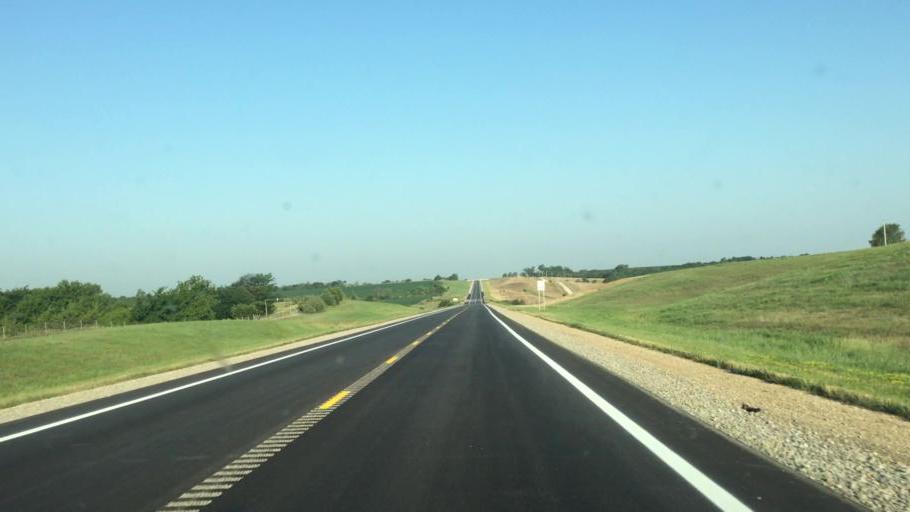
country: US
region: Kansas
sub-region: Doniphan County
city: Highland
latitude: 39.8412
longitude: -95.3707
